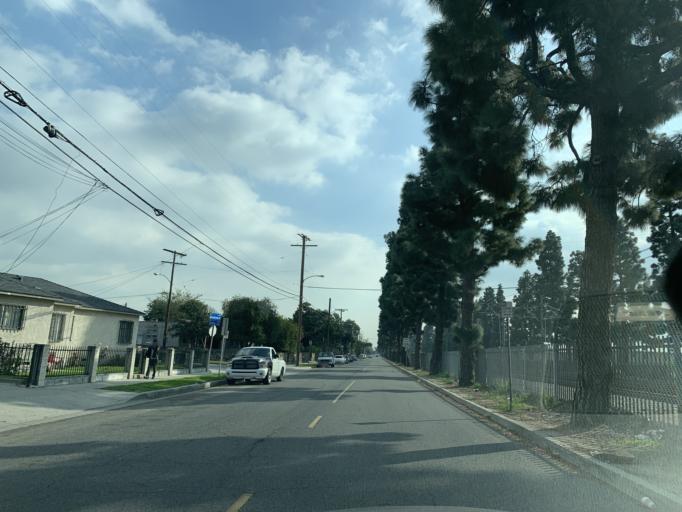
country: US
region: California
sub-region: Los Angeles County
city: Willowbrook
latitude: 33.9236
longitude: -118.2351
